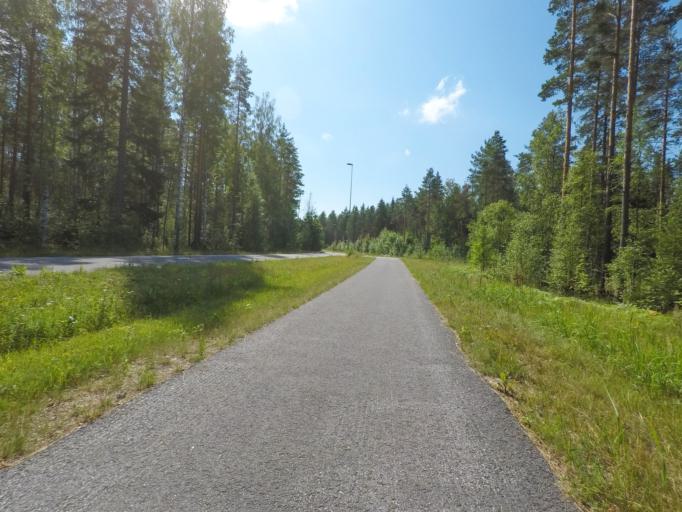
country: FI
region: Southern Savonia
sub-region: Mikkeli
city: Puumala
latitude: 61.5143
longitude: 28.1642
